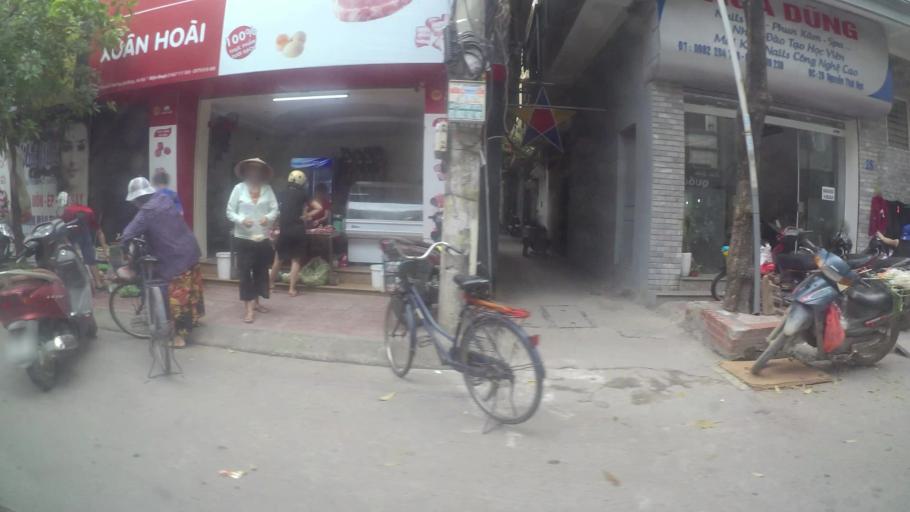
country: VN
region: Ha Noi
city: Ha Dong
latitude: 20.9730
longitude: 105.7751
